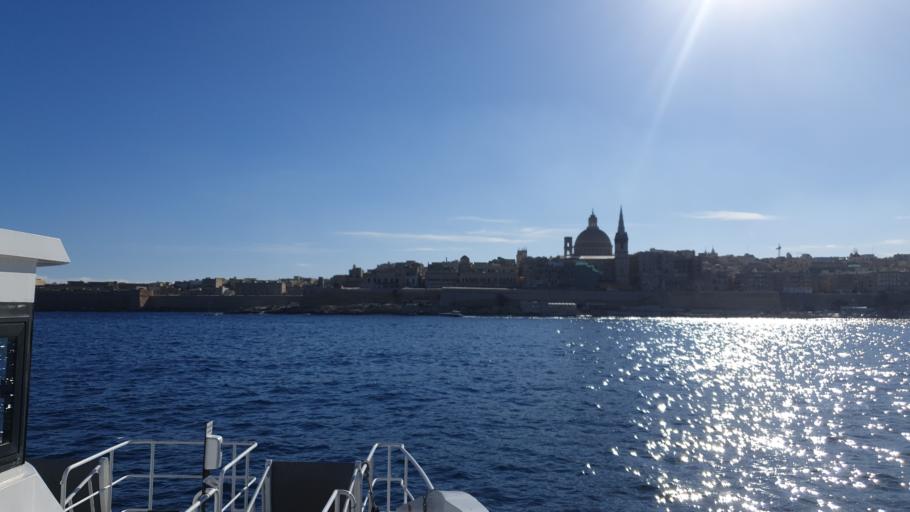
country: MT
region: Il-Belt Valletta
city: Valletta
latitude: 35.9030
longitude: 14.5092
